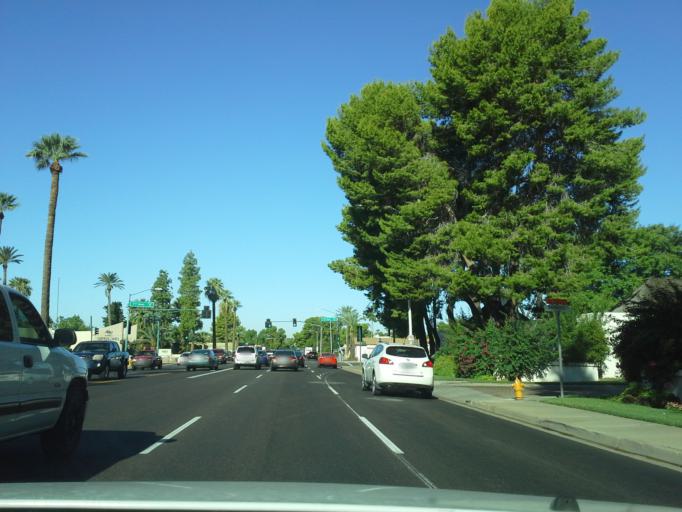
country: US
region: Arizona
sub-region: Maricopa County
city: Phoenix
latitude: 33.5384
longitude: -112.0814
